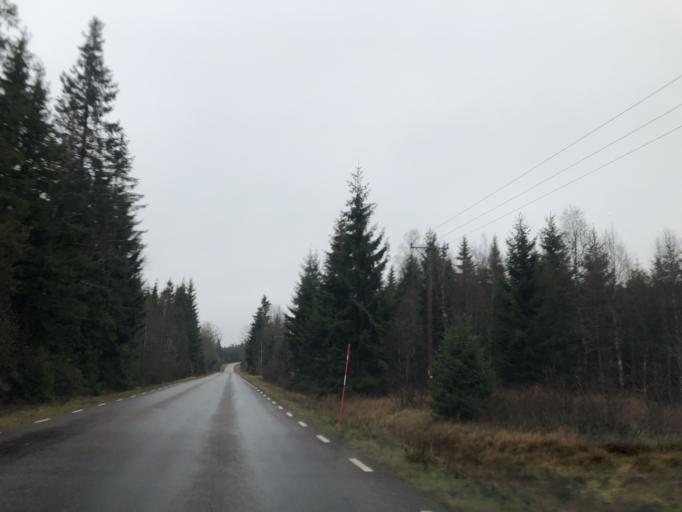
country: SE
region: Vaestra Goetaland
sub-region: Ulricehamns Kommun
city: Ulricehamn
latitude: 57.7474
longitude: 13.5284
